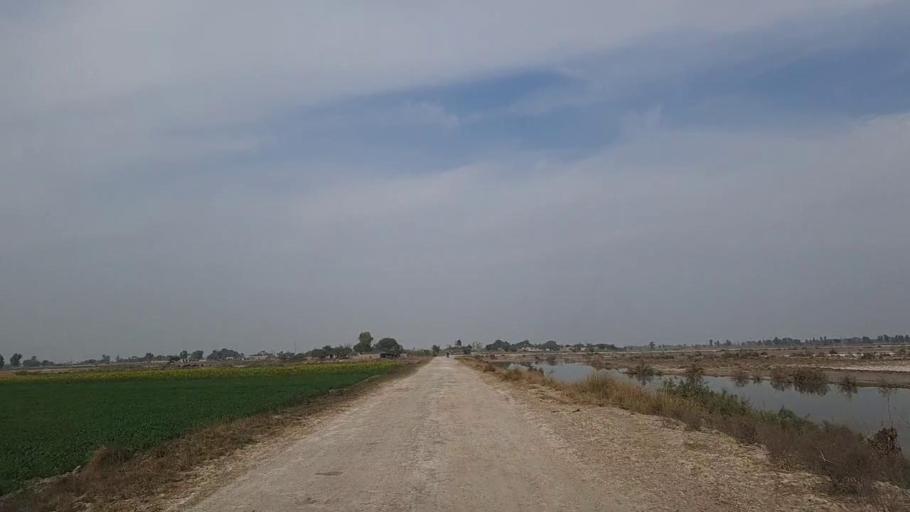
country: PK
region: Sindh
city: Daur
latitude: 26.4754
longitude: 68.4024
